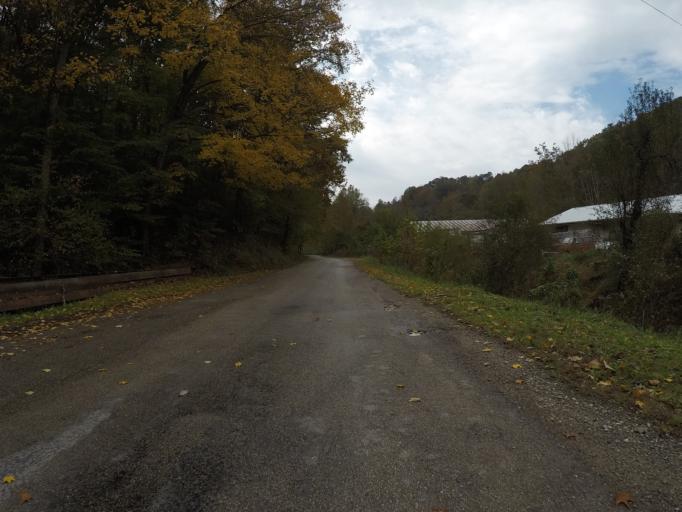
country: US
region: West Virginia
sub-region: Wayne County
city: Lavalette
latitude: 38.3401
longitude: -82.4358
